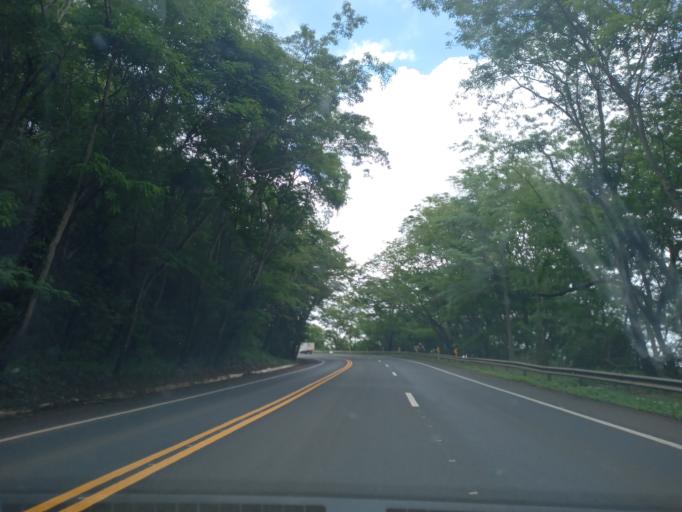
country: BR
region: Minas Gerais
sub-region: Monte Carmelo
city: Monte Carmelo
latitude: -19.2629
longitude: -47.6455
